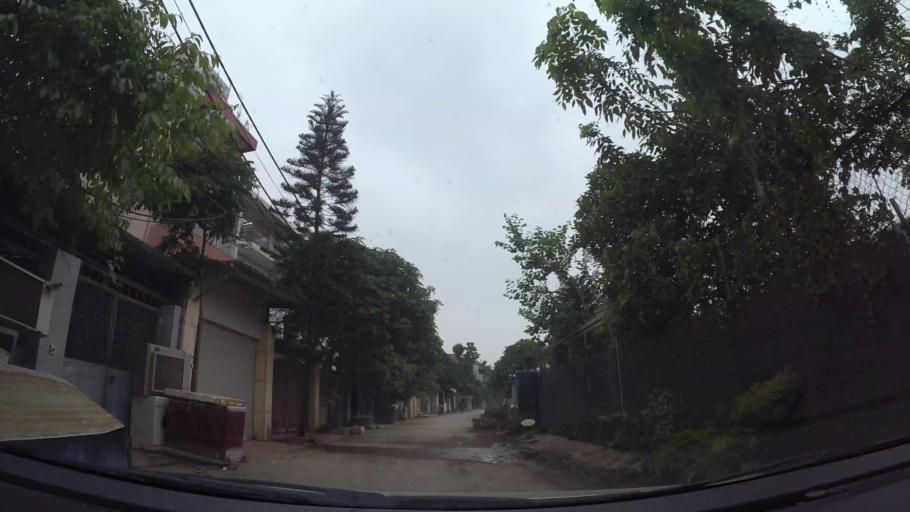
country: VN
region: Ha Noi
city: Tay Ho
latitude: 21.0766
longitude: 105.8263
